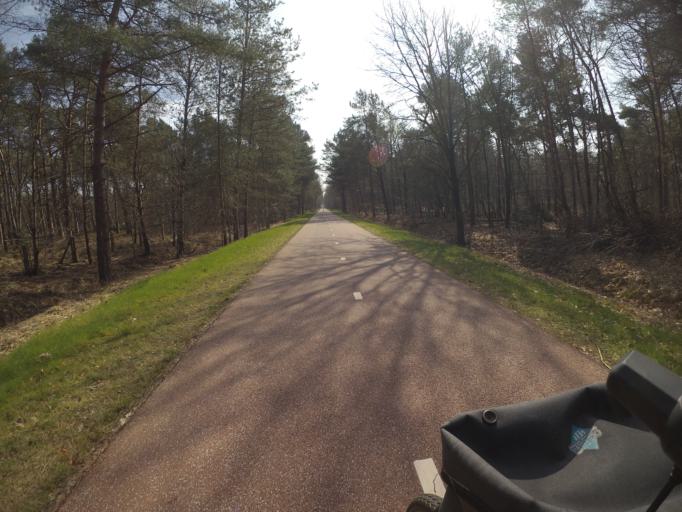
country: NL
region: North Brabant
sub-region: Gemeente Goirle
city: Goirle
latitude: 51.5505
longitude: 5.0231
